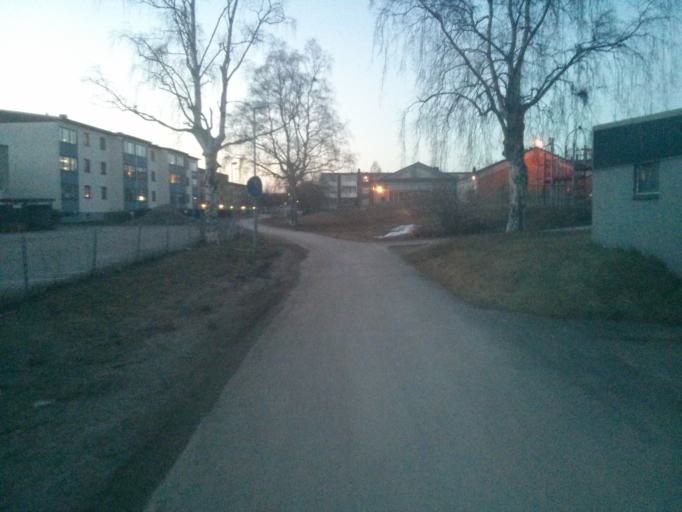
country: SE
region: Vaesternorrland
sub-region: Sundsvalls Kommun
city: Kvissleby
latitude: 62.2981
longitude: 17.3800
